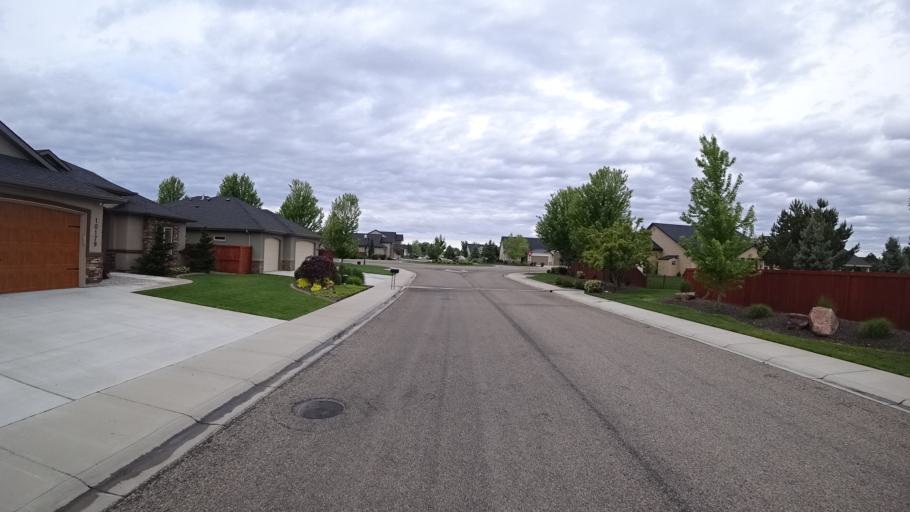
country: US
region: Idaho
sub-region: Ada County
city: Star
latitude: 43.6997
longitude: -116.4805
